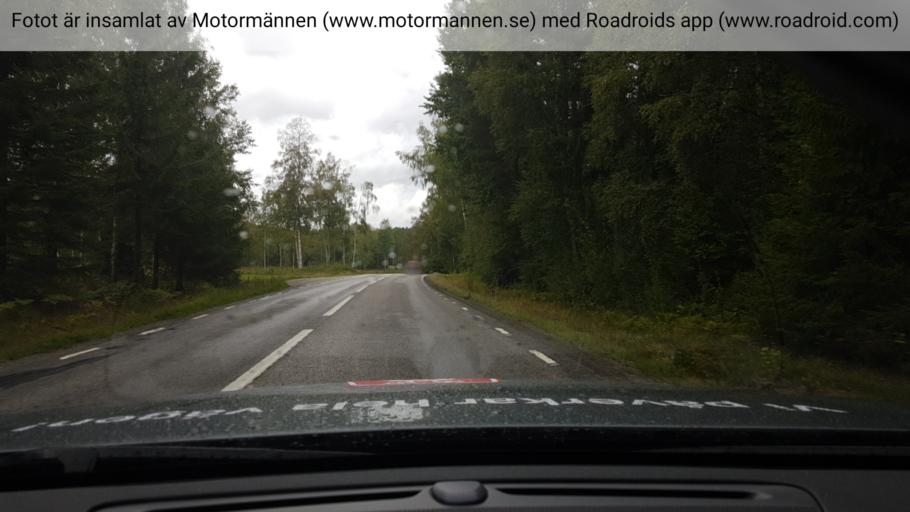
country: SE
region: Stockholm
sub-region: Botkyrka Kommun
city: Tullinge
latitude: 59.1234
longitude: 17.8820
